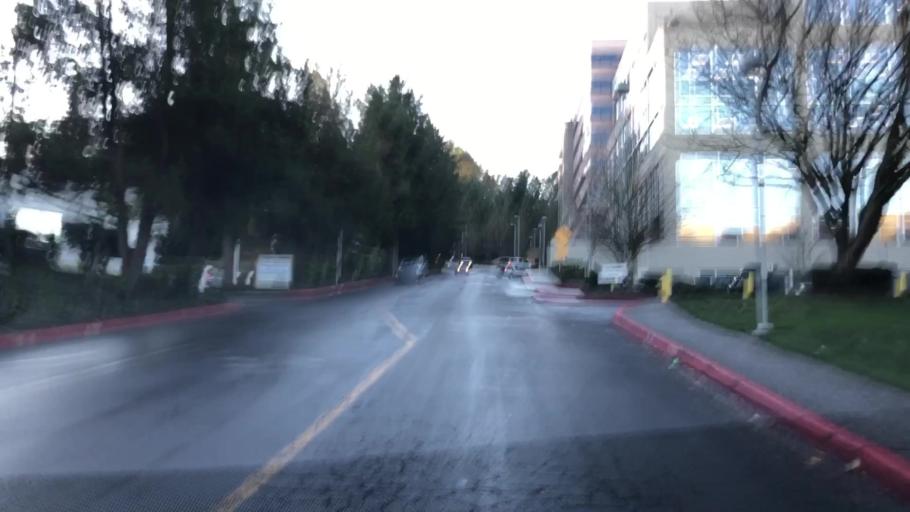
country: US
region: Washington
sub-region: King County
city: Newport
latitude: 47.5794
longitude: -122.1646
